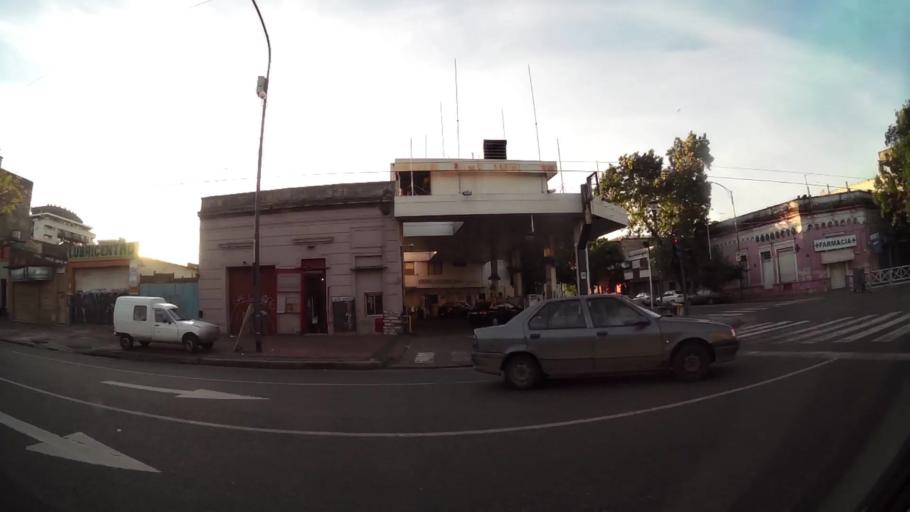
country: AR
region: Buenos Aires F.D.
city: Buenos Aires
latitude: -34.6430
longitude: -58.4132
